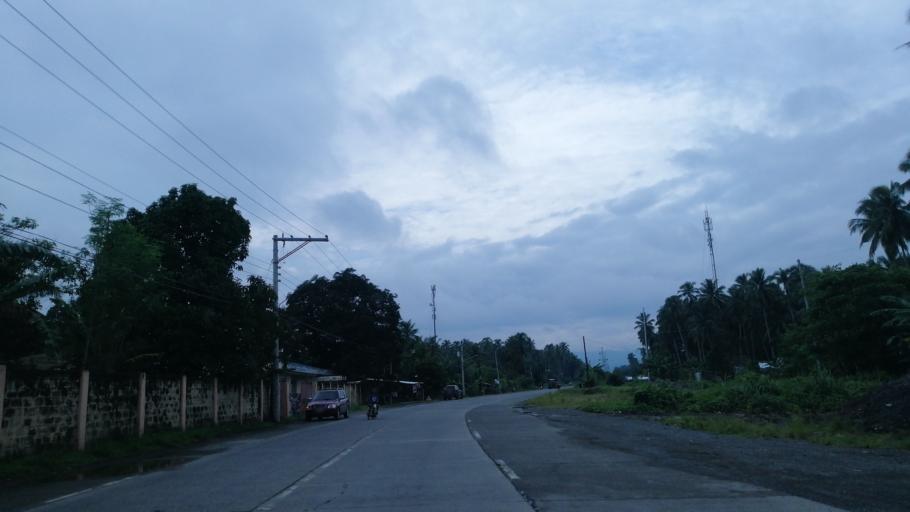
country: PH
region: Davao
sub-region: Province of Davao del Norte
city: Corocotan
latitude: 7.3991
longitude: 125.7731
